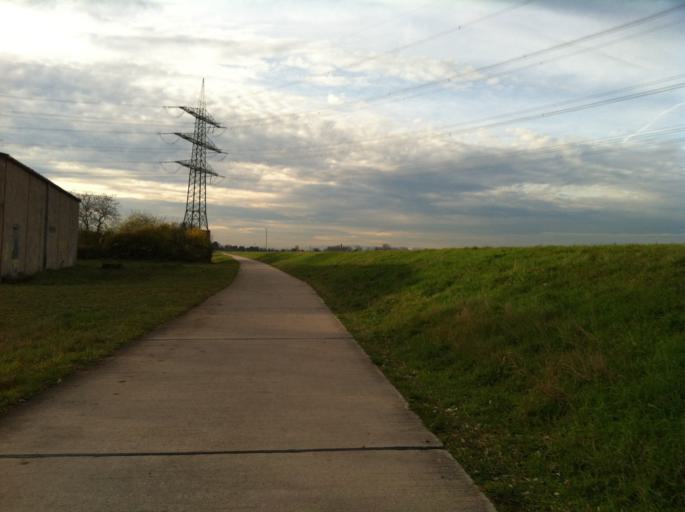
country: DE
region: Hesse
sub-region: Regierungsbezirk Darmstadt
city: Bischofsheim
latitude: 49.9963
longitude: 8.3759
